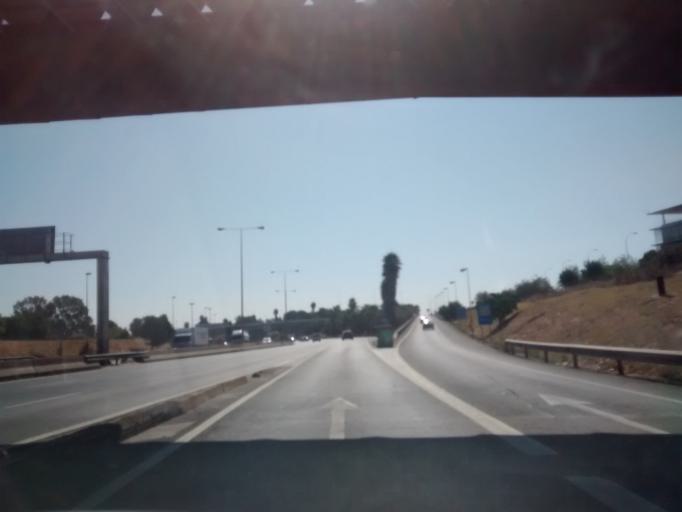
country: ES
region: Andalusia
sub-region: Provincia de Sevilla
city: Sevilla
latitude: 37.3403
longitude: -5.9771
